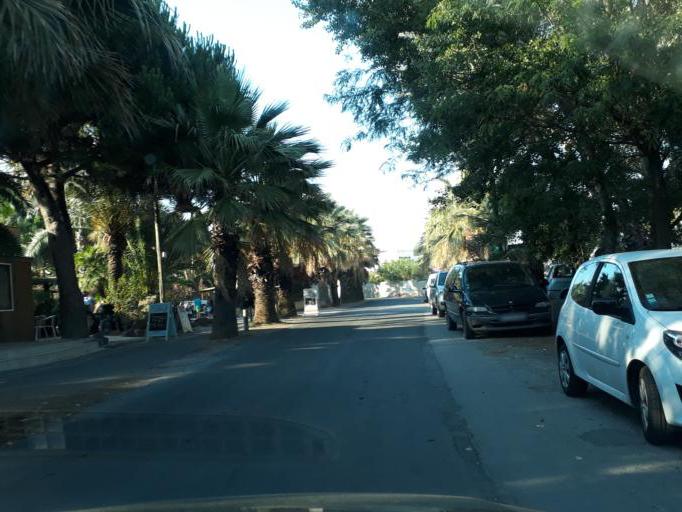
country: FR
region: Languedoc-Roussillon
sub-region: Departement de l'Herault
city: Agde
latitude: 43.2843
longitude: 3.4743
